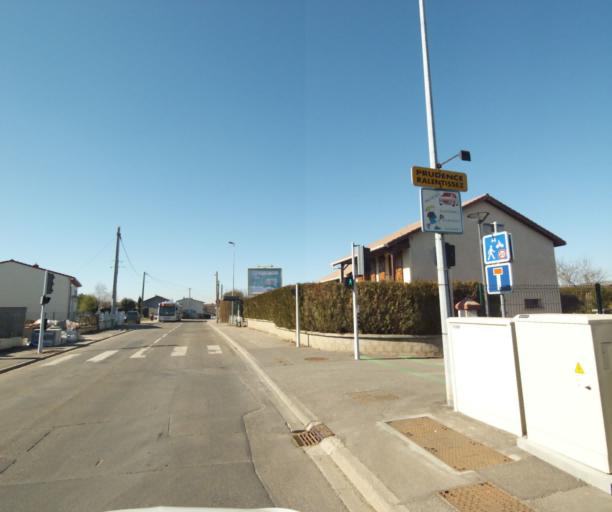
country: FR
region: Lorraine
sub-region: Departement de Meurthe-et-Moselle
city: Tomblaine
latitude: 48.6840
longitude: 6.2298
